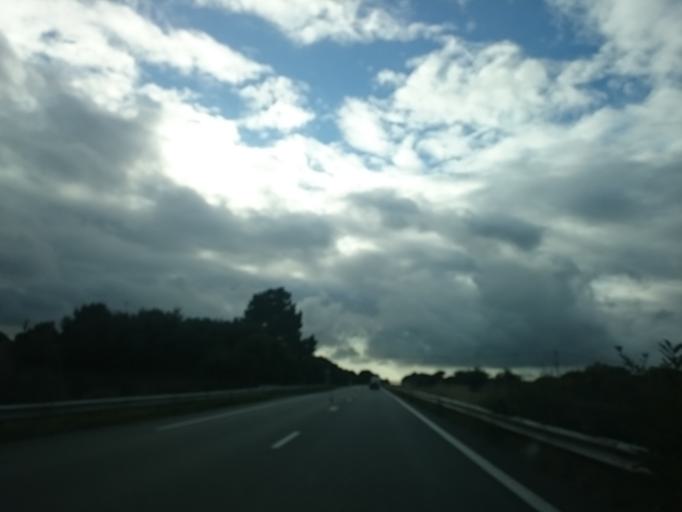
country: FR
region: Brittany
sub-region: Departement du Finistere
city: Guerlesquin
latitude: 48.5685
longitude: -3.5955
